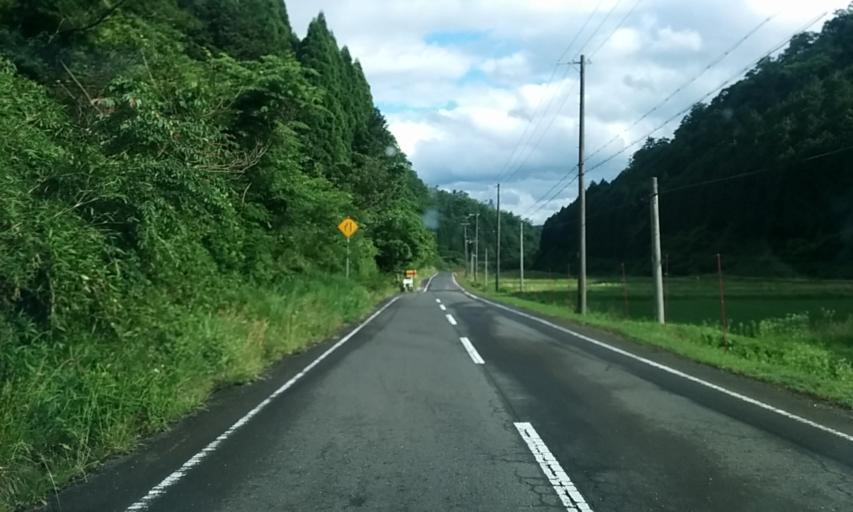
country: JP
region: Kyoto
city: Ayabe
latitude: 35.3704
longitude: 135.2878
